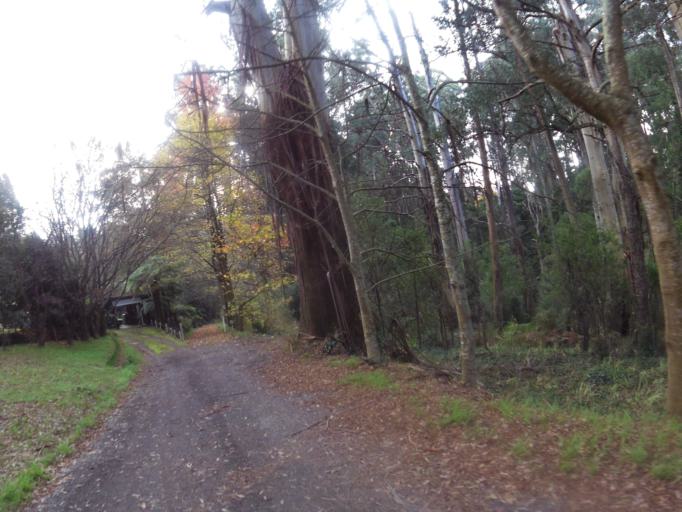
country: AU
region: Victoria
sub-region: Yarra Ranges
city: Kallista
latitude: -37.8719
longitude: 145.3508
